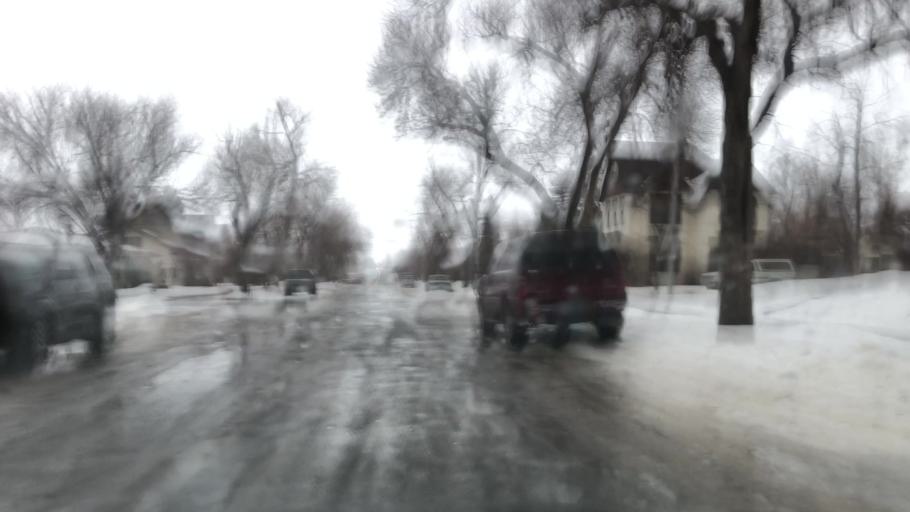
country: US
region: Montana
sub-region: Lewis and Clark County
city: Helena
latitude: 46.5887
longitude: -112.0190
